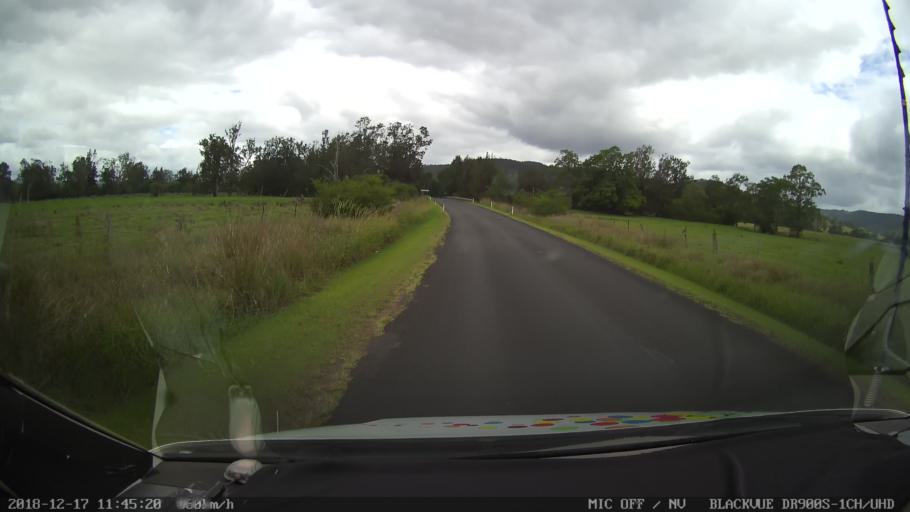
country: AU
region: New South Wales
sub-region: Kyogle
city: Kyogle
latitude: -28.6452
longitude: 152.5960
